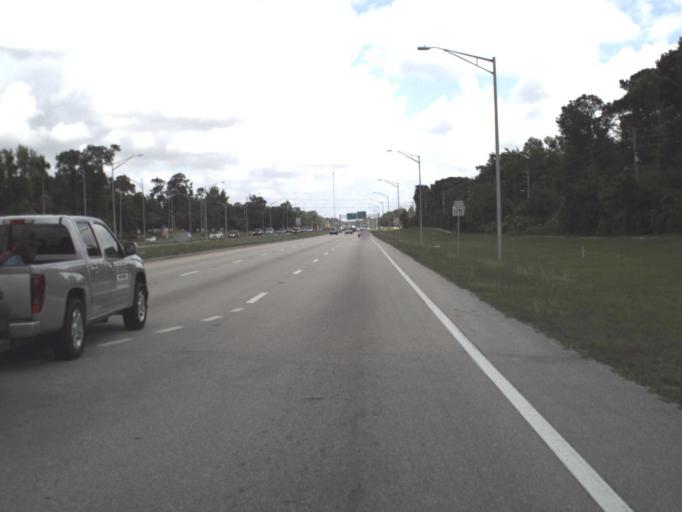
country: US
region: Florida
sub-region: Duval County
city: Jacksonville
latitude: 30.2303
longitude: -81.5519
